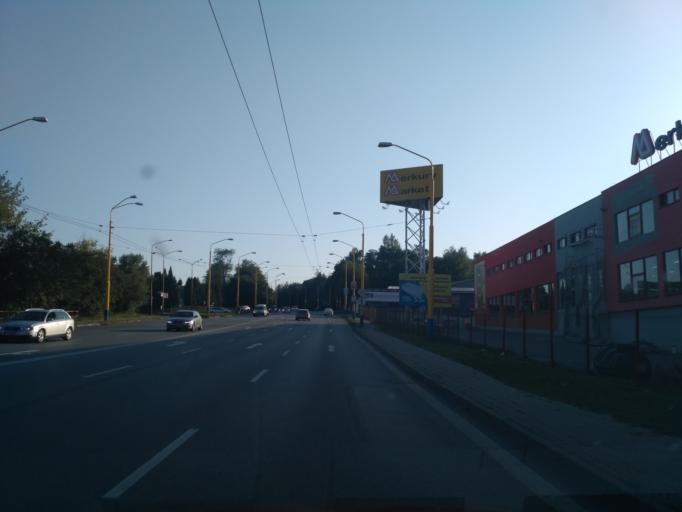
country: SK
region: Presovsky
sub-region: Okres Presov
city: Presov
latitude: 49.0063
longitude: 21.2466
